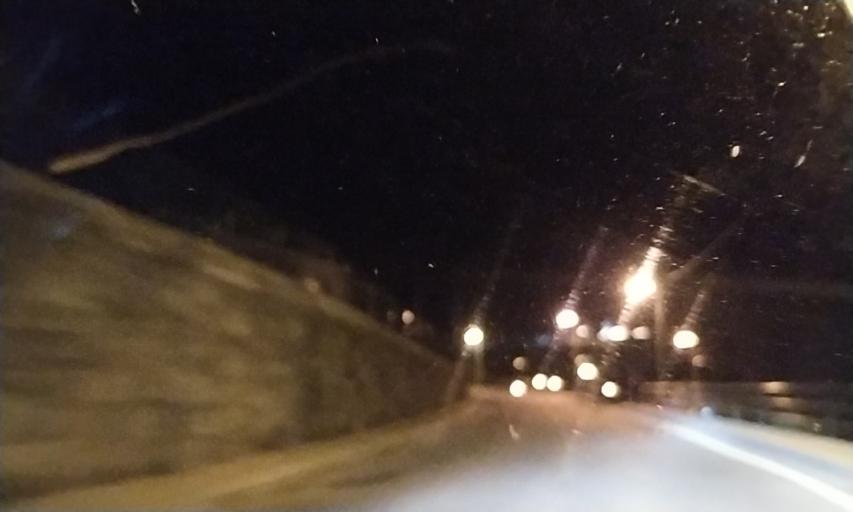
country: PT
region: Castelo Branco
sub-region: Concelho do Fundao
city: Fundao
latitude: 40.1353
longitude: -7.5057
